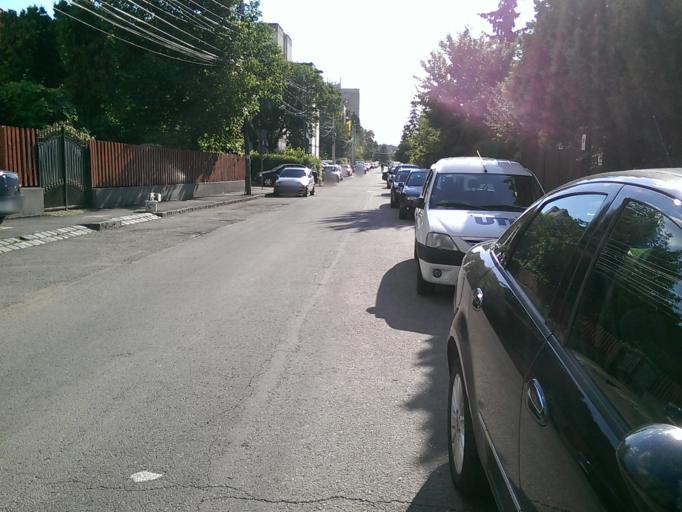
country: RO
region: Cluj
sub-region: Municipiul Cluj-Napoca
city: Cluj-Napoca
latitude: 46.7647
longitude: 23.6170
